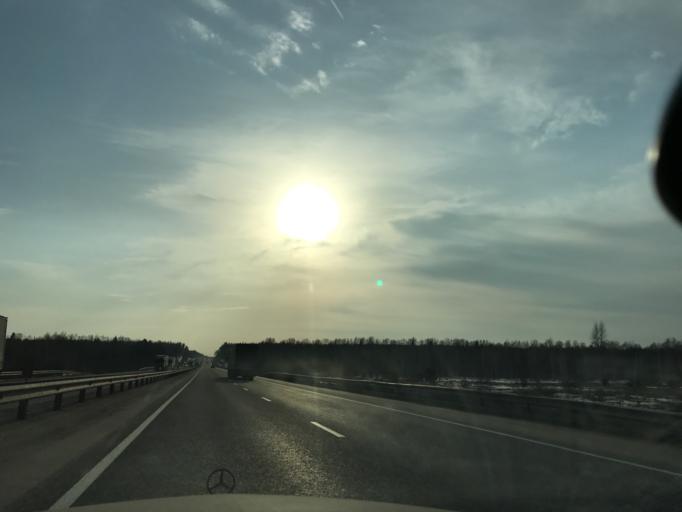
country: RU
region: Vladimir
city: Sudogda
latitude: 56.1265
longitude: 40.8687
